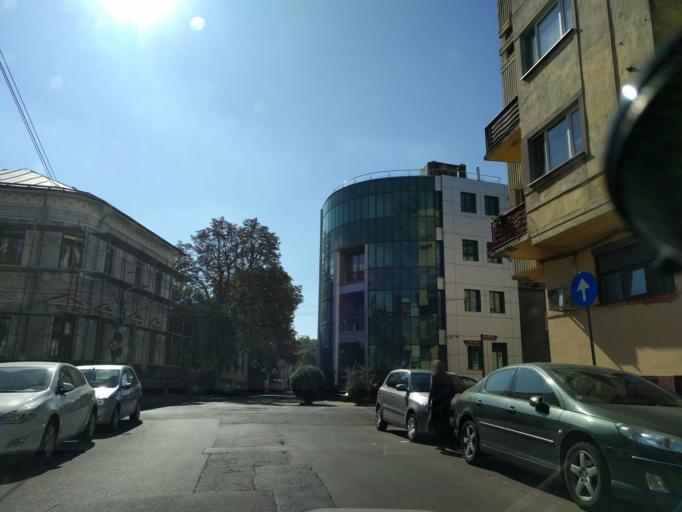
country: RO
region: Bucuresti
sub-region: Municipiul Bucuresti
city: Bucharest
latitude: 44.4313
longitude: 26.1146
